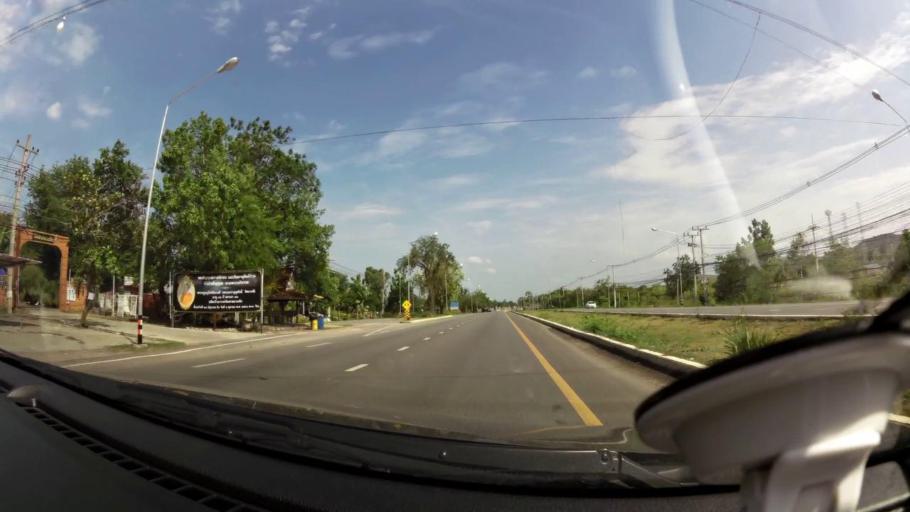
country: TH
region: Prachuap Khiri Khan
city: Hua Hin
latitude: 12.5181
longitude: 99.9650
